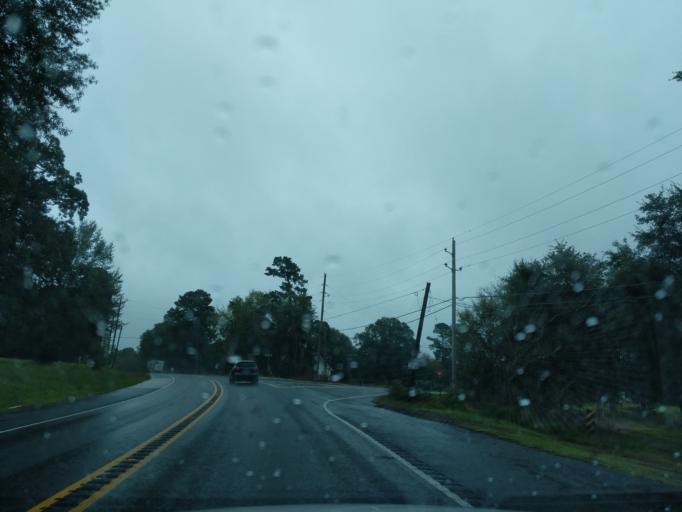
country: US
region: Louisiana
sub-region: Caddo Parish
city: Greenwood
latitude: 32.3741
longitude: -94.0346
